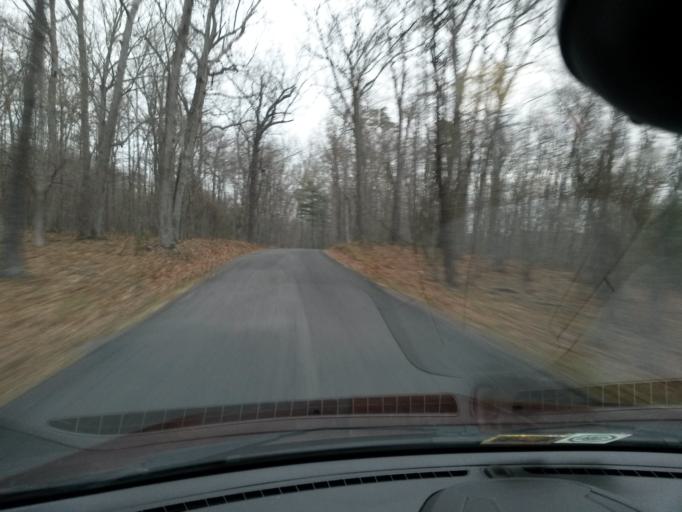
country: US
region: Virginia
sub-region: Bath County
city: Warm Springs
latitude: 38.0255
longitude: -79.7066
